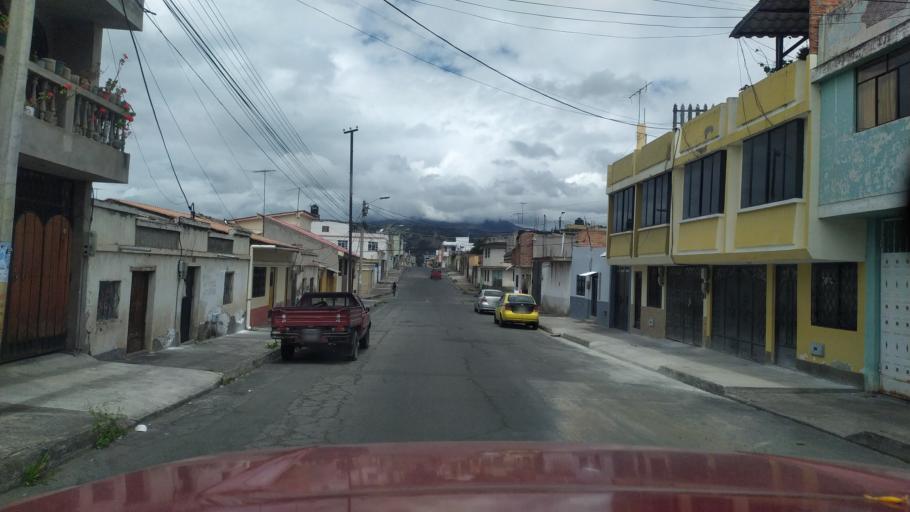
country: EC
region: Chimborazo
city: Riobamba
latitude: -1.6663
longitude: -78.6405
